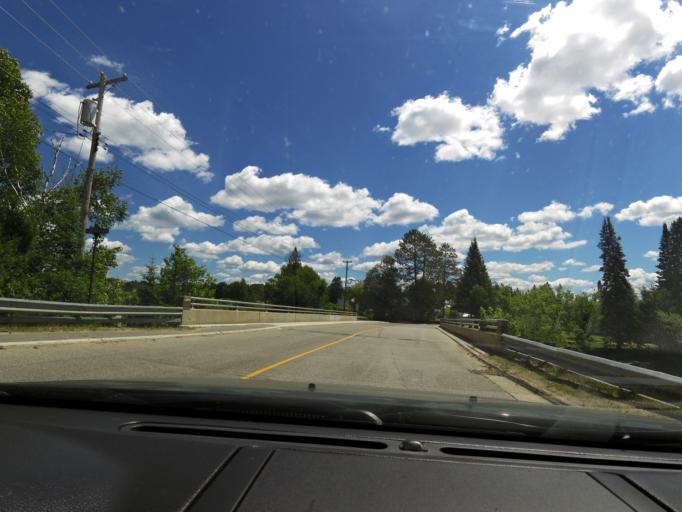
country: CA
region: Ontario
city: Huntsville
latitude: 45.5575
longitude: -79.2259
